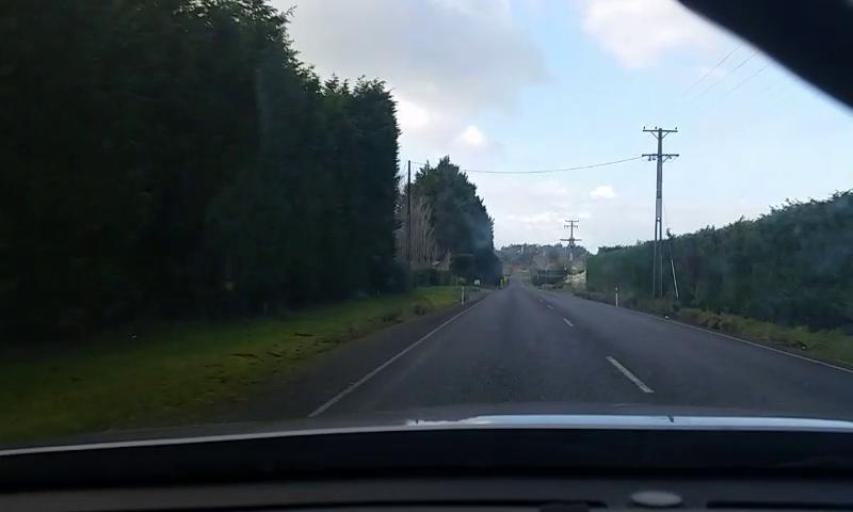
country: NZ
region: Southland
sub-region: Invercargill City
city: Invercargill
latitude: -46.3806
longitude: 168.4315
